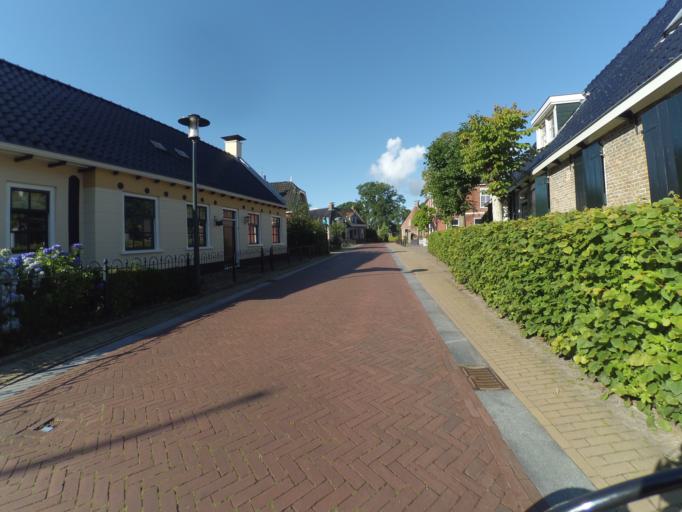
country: NL
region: Friesland
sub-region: Gemeente Kollumerland en Nieuwkruisland
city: Kollumerzwaag
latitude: 53.2641
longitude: 6.1054
